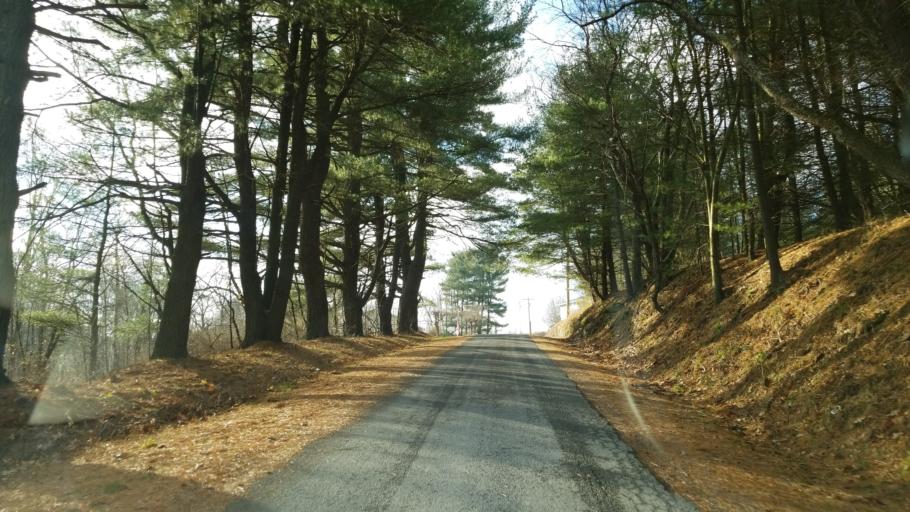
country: US
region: Pennsylvania
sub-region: Clearfield County
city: DuBois
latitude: 41.1105
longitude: -78.7262
